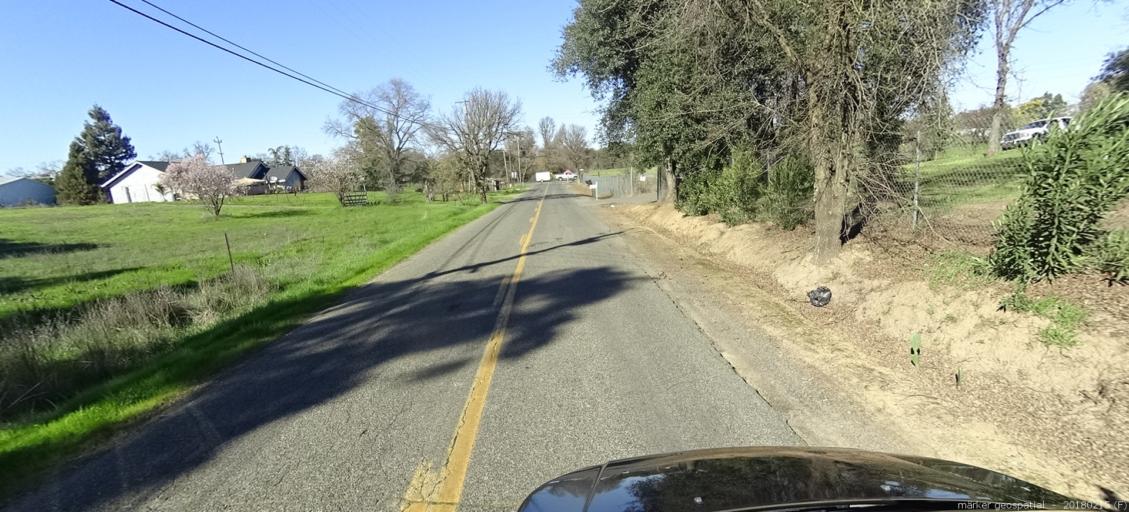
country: US
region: California
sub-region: Sacramento County
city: Rio Linda
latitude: 38.6967
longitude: -121.4199
